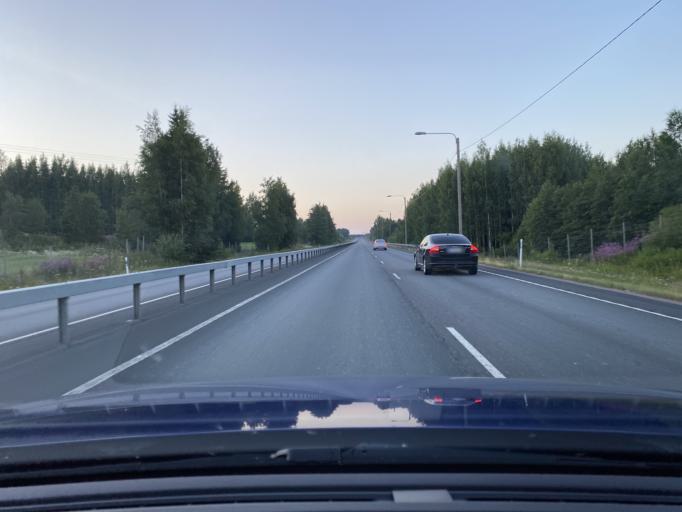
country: FI
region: Pirkanmaa
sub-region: Luoteis-Pirkanmaa
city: Parkano
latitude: 61.8799
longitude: 22.9707
